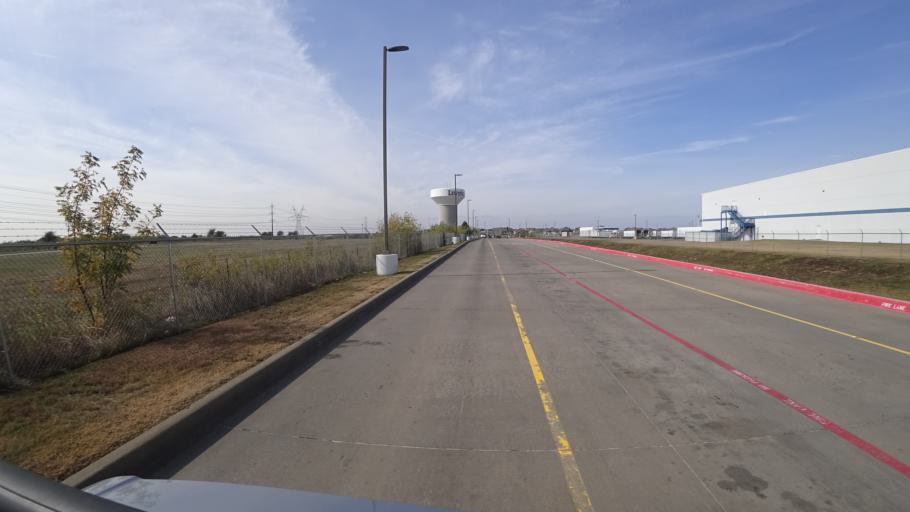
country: US
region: Texas
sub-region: Denton County
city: The Colony
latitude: 33.0622
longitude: -96.8726
